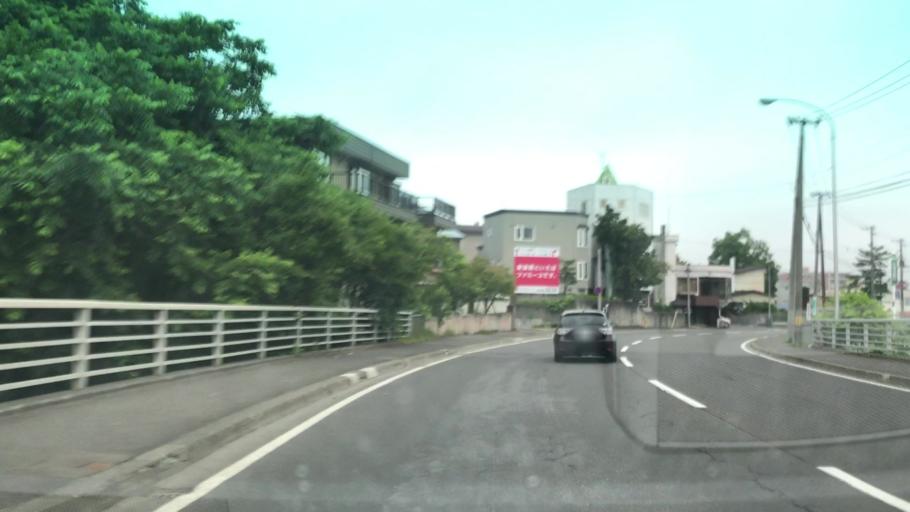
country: JP
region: Hokkaido
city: Sapporo
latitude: 43.0006
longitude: 141.3321
